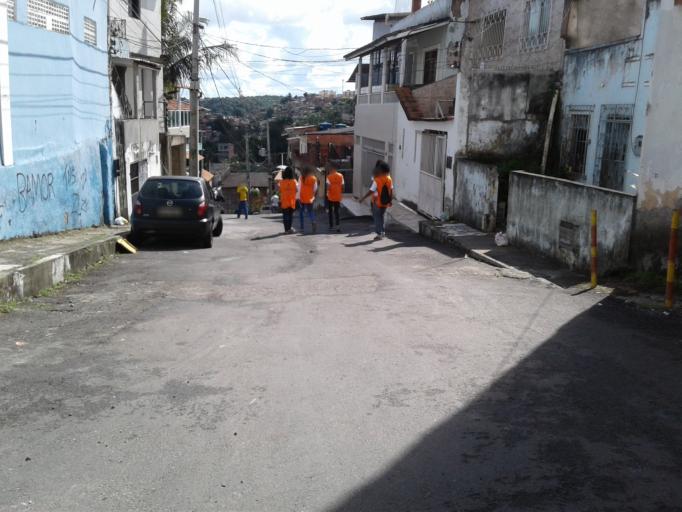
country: BR
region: Bahia
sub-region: Salvador
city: Salvador
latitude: -12.9119
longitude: -38.4706
